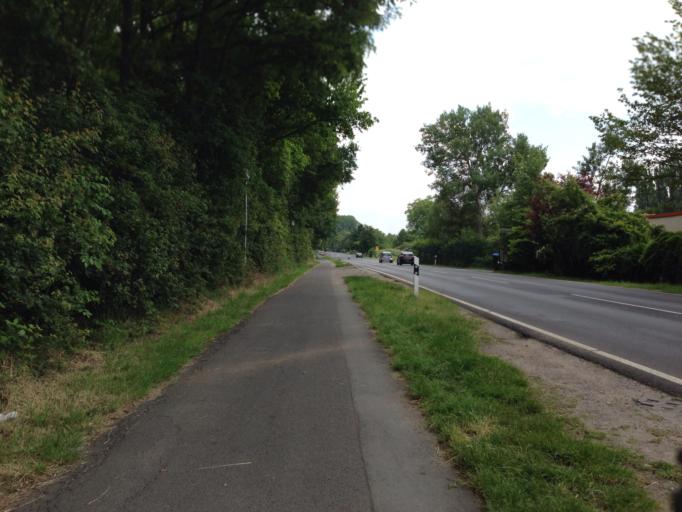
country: DE
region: Hesse
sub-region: Regierungsbezirk Darmstadt
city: Hanau am Main
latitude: 50.1288
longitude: 8.8758
